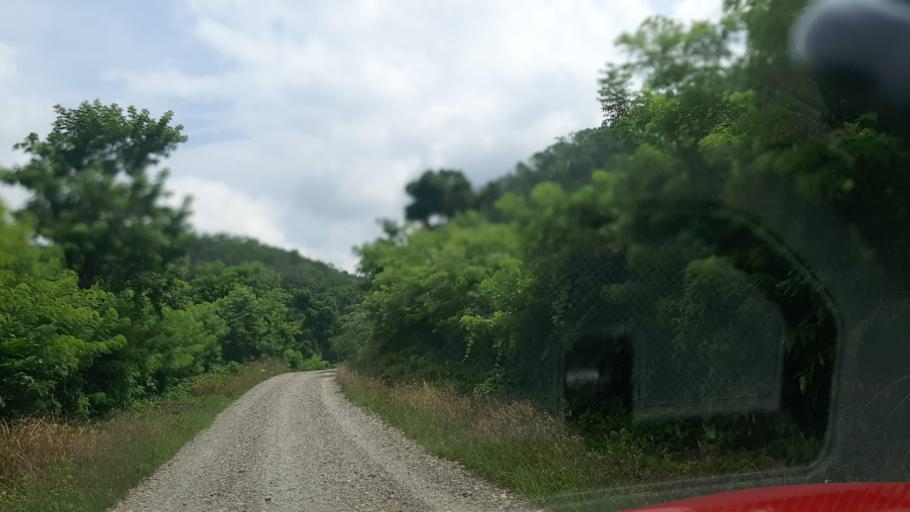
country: MX
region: Veracruz
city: Gutierrez Zamora
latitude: 20.4533
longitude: -97.1772
